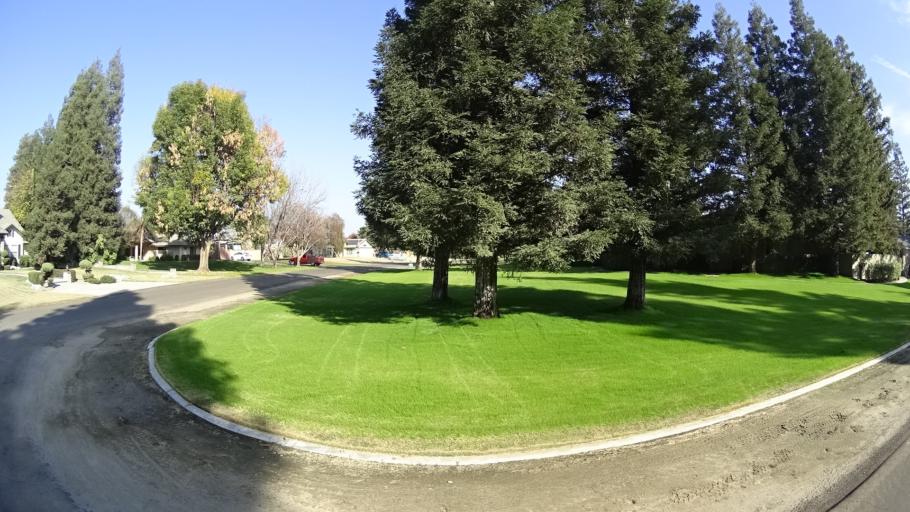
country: US
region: California
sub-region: Kern County
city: Rosedale
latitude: 35.3639
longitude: -119.1753
